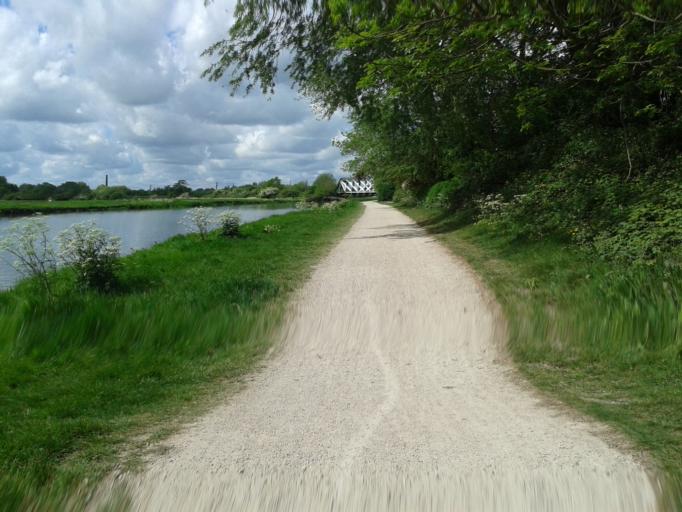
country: GB
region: England
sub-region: Cambridgeshire
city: Cambridge
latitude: 52.2209
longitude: 0.1603
